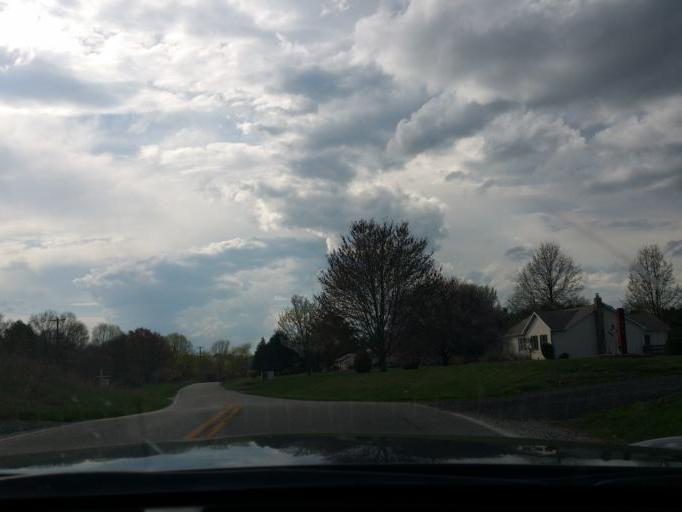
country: US
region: Maryland
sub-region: Cecil County
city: Rising Sun
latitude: 39.6381
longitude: -76.1133
